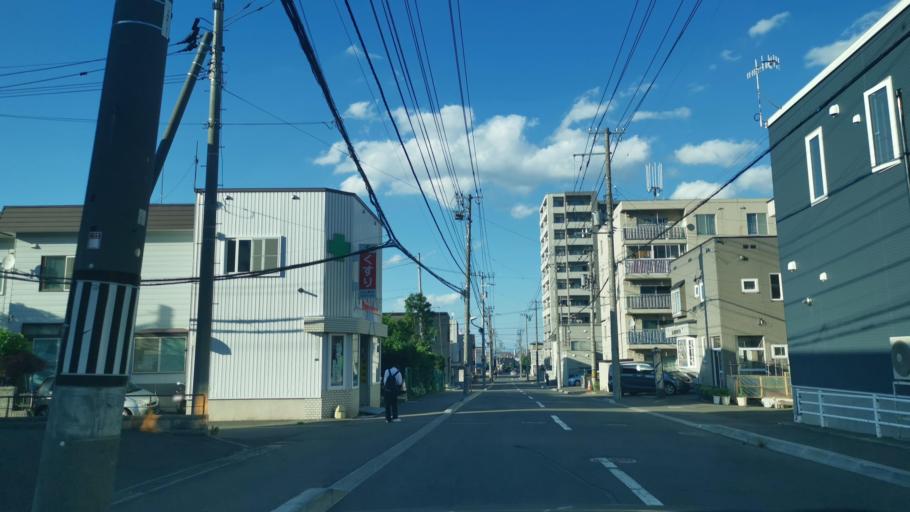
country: JP
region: Hokkaido
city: Sapporo
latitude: 43.0940
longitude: 141.2671
